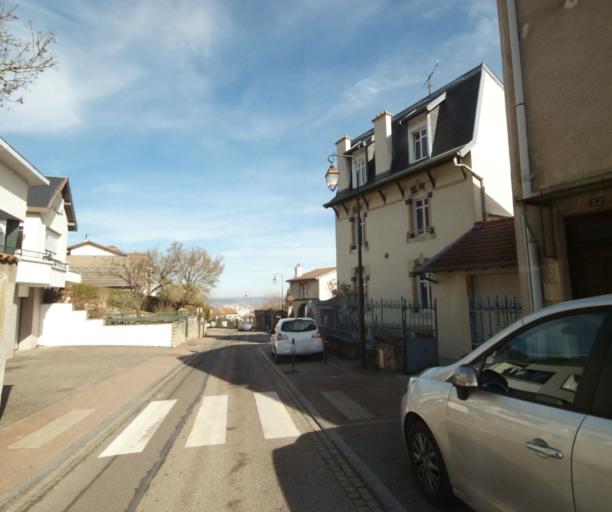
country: FR
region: Lorraine
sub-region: Departement de Meurthe-et-Moselle
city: Villers-les-Nancy
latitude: 48.6586
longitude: 6.1657
